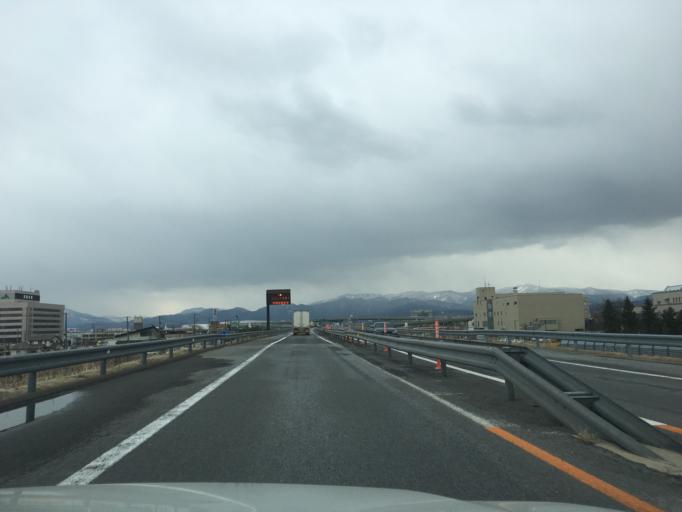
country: JP
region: Aomori
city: Aomori Shi
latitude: 40.7970
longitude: 140.7355
